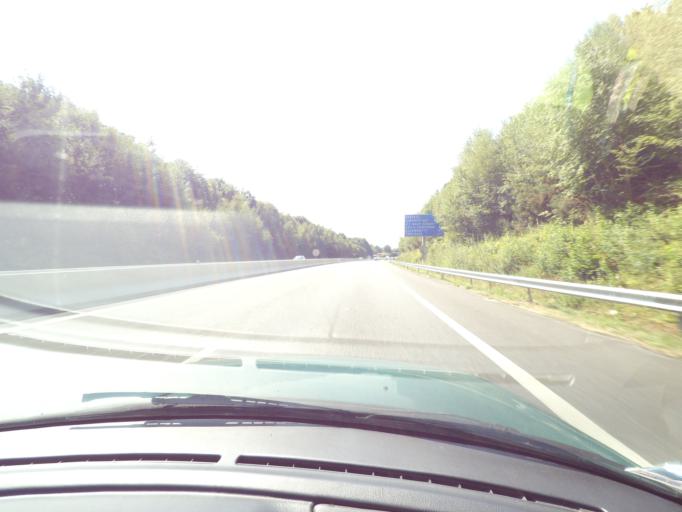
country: FR
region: Limousin
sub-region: Departement de la Haute-Vienne
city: Le Palais-sur-Vienne
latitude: 45.8645
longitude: 1.2874
